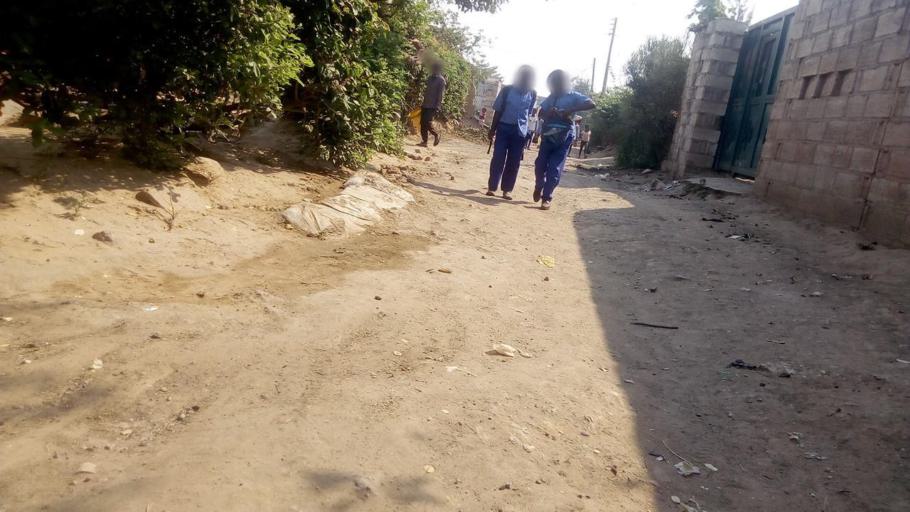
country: ZM
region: Lusaka
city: Lusaka
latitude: -15.3567
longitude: 28.2876
